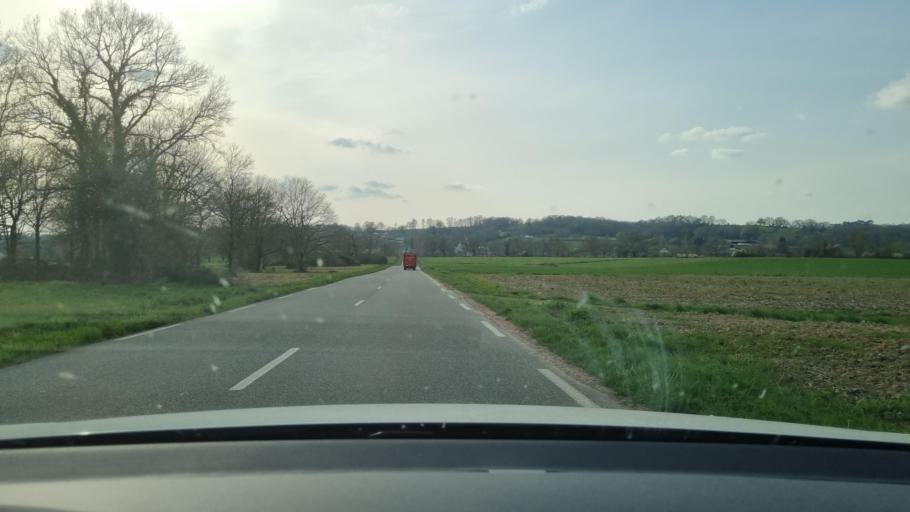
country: FR
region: Aquitaine
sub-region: Departement des Pyrenees-Atlantiques
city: Soumoulou
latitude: 43.3774
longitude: -0.1189
